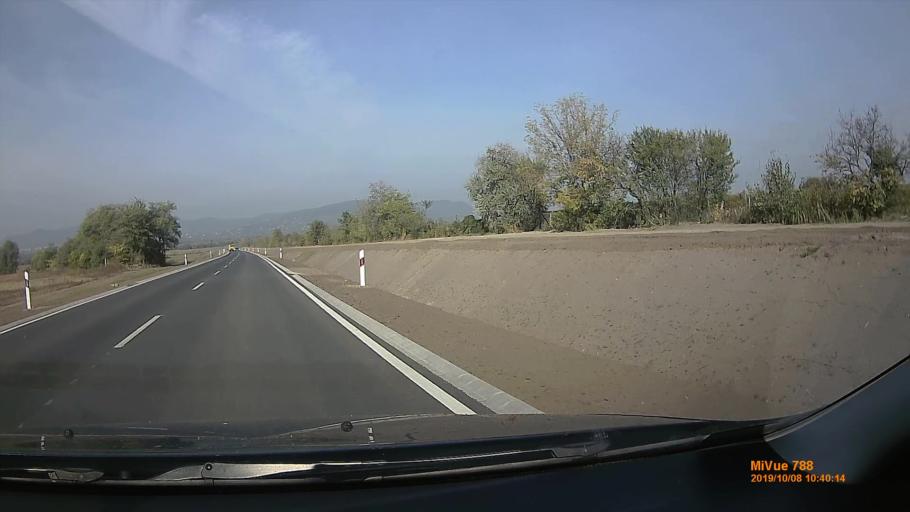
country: HU
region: Pest
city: Dunakeszi
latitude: 47.6604
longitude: 19.1485
